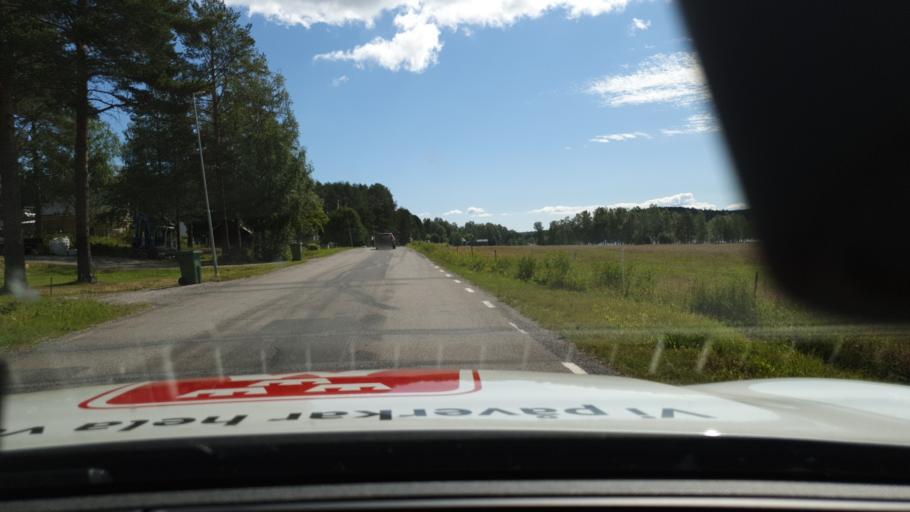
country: SE
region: Norrbotten
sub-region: Lulea Kommun
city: Ranea
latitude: 65.7746
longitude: 22.2408
